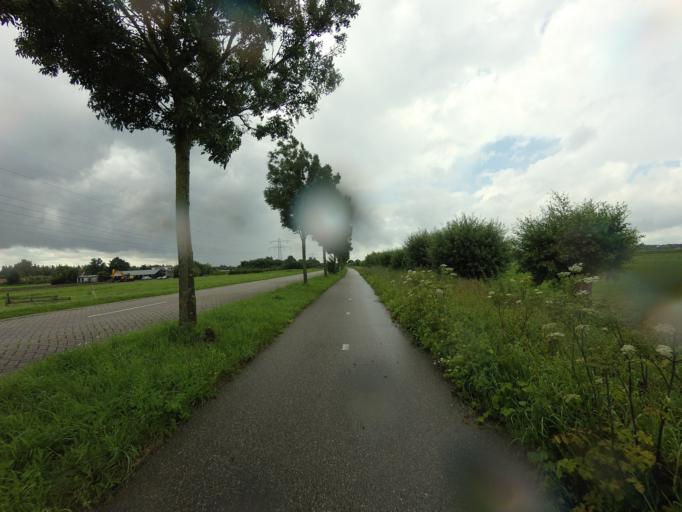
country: NL
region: Utrecht
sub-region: Gemeente Utrecht
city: Utrecht
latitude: 52.1424
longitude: 5.1168
